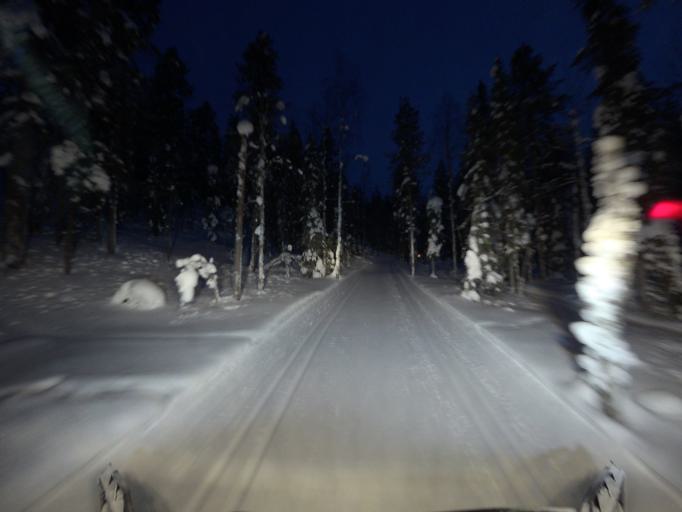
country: FI
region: Lapland
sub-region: Tunturi-Lappi
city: Kolari
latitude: 67.5981
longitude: 24.1109
